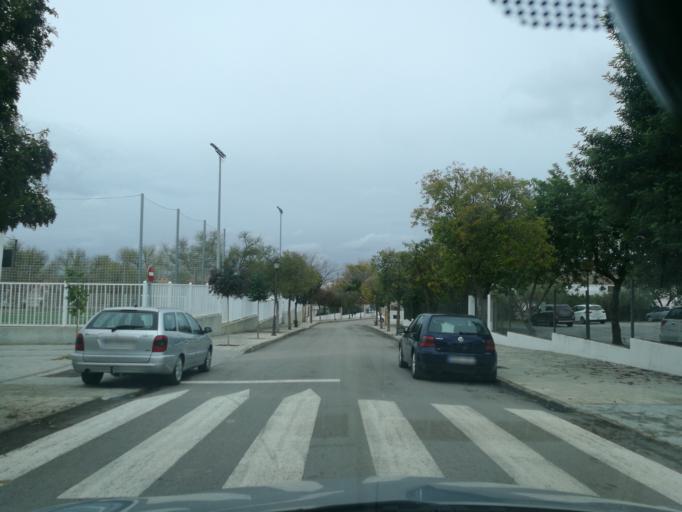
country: ES
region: Andalusia
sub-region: Provincia de Sevilla
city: La Campana
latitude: 37.5646
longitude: -5.4281
